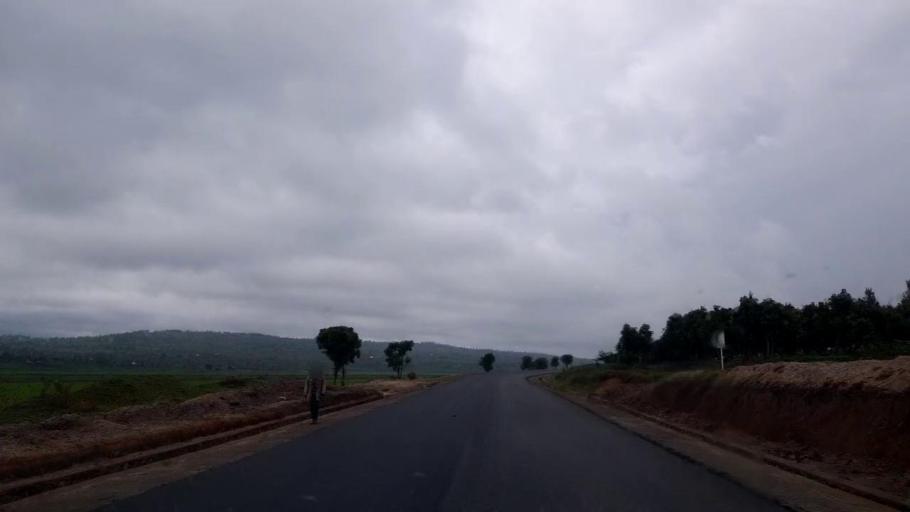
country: RW
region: Northern Province
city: Byumba
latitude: -1.4078
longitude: 30.2851
